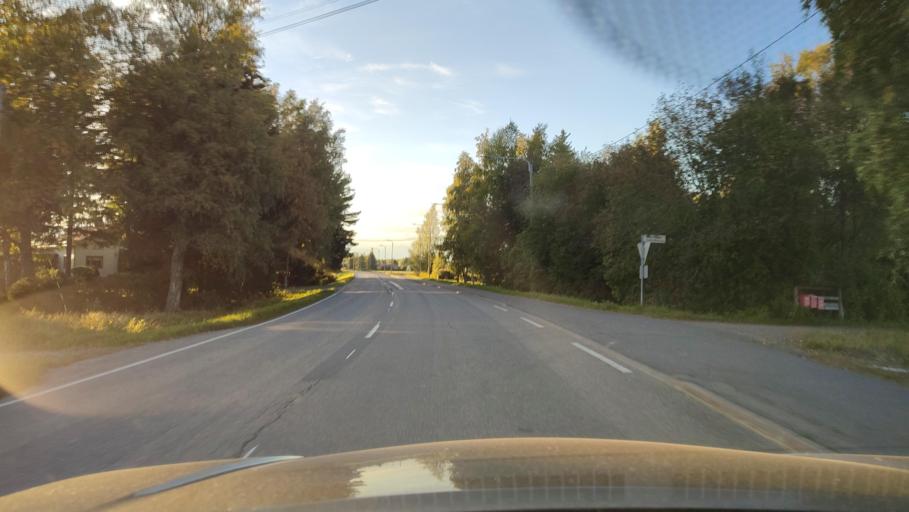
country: FI
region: Ostrobothnia
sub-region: Sydosterbotten
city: Kristinestad
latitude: 62.2561
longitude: 21.4993
